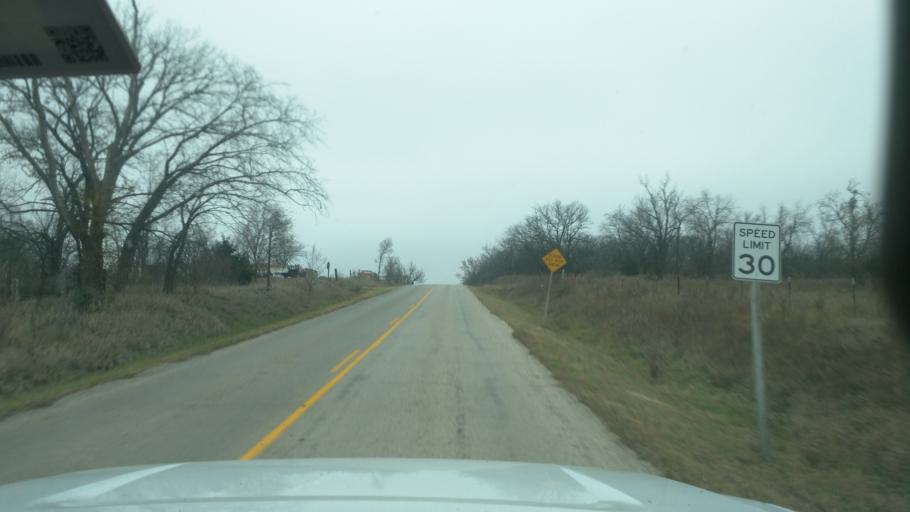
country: US
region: Kansas
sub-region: Morris County
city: Council Grove
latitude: 38.6453
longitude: -96.2615
